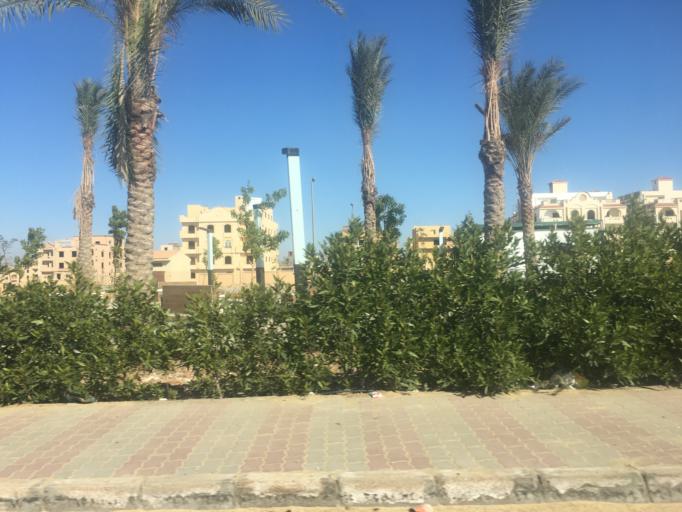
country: EG
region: Al Jizah
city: Awsim
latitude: 30.0141
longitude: 30.9774
